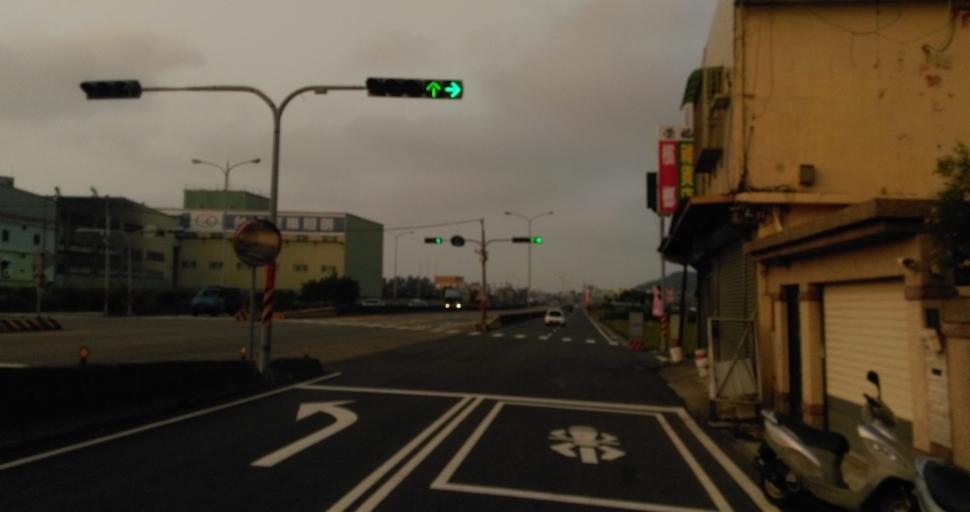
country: TW
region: Taiwan
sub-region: Hsinchu
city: Zhubei
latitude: 24.8680
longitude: 120.9535
